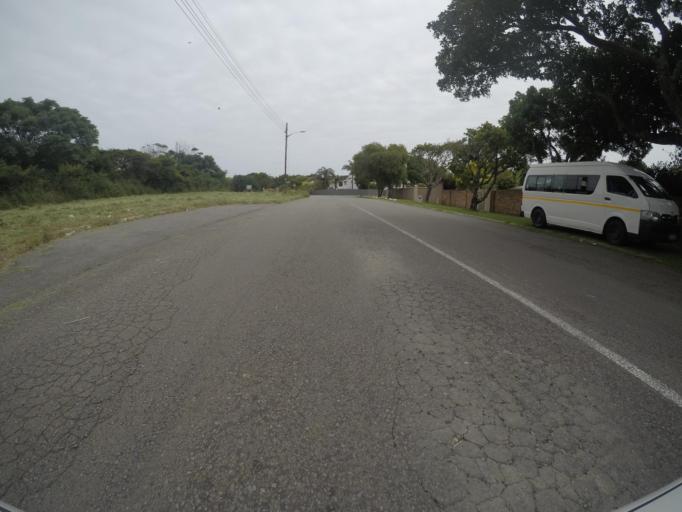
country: ZA
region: Eastern Cape
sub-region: Buffalo City Metropolitan Municipality
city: East London
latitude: -32.9761
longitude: 27.9436
